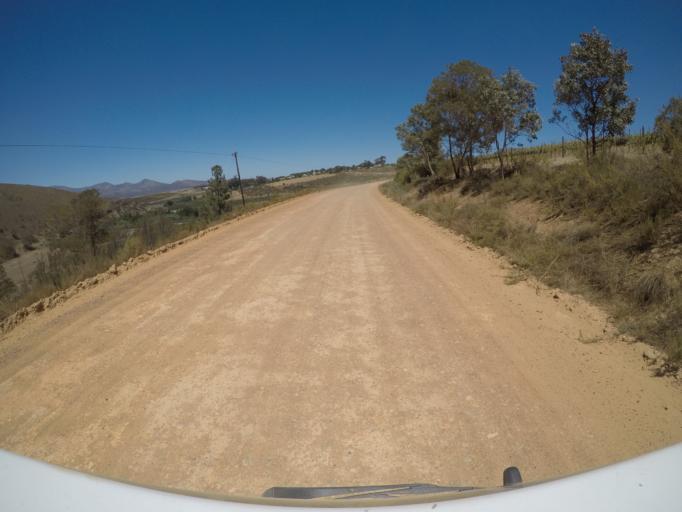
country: ZA
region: Western Cape
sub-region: Overberg District Municipality
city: Hermanus
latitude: -34.2164
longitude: 19.2089
